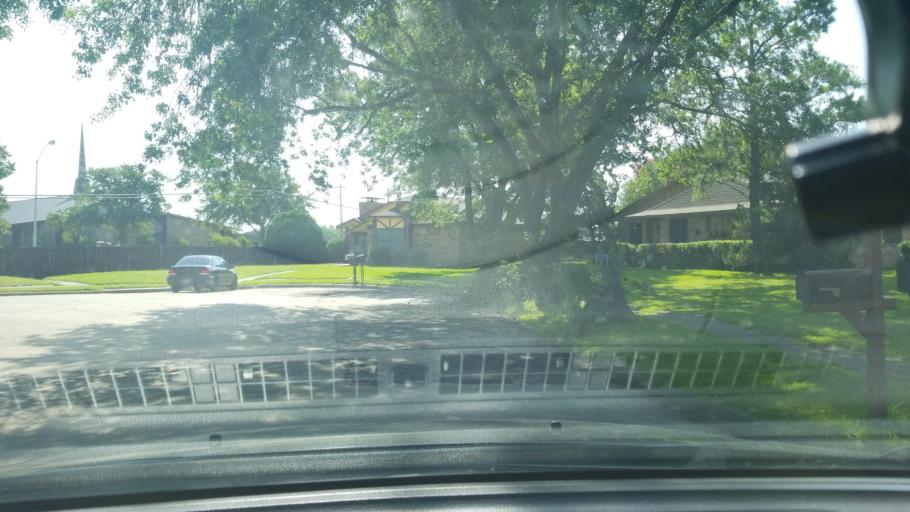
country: US
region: Texas
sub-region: Dallas County
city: Mesquite
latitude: 32.8202
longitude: -96.6188
